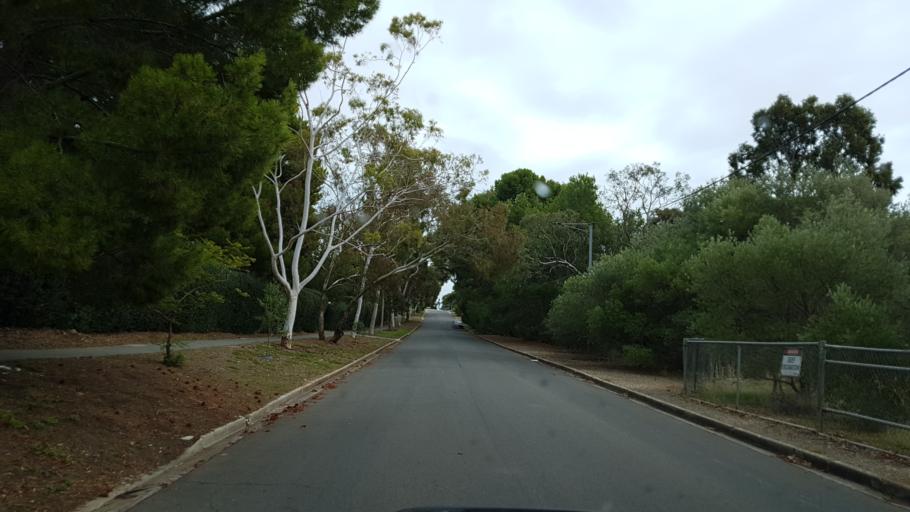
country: AU
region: South Australia
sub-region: Mitcham
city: Mitcham
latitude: -34.9833
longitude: 138.6220
